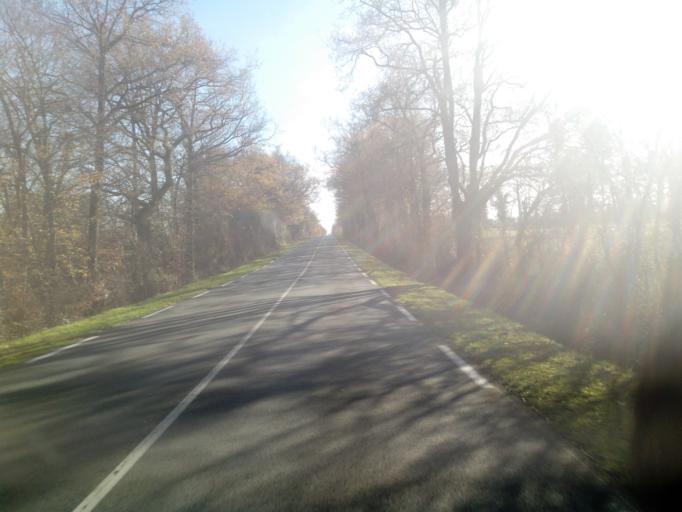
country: FR
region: Limousin
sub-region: Departement de la Haute-Vienne
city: Bussiere-Poitevine
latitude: 46.2795
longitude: 0.8556
